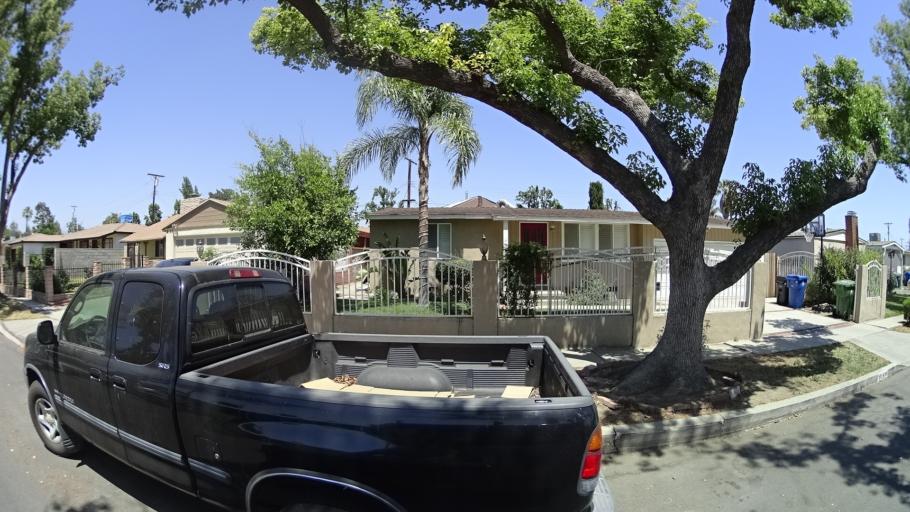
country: US
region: California
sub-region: Los Angeles County
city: Van Nuys
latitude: 34.2194
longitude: -118.4356
